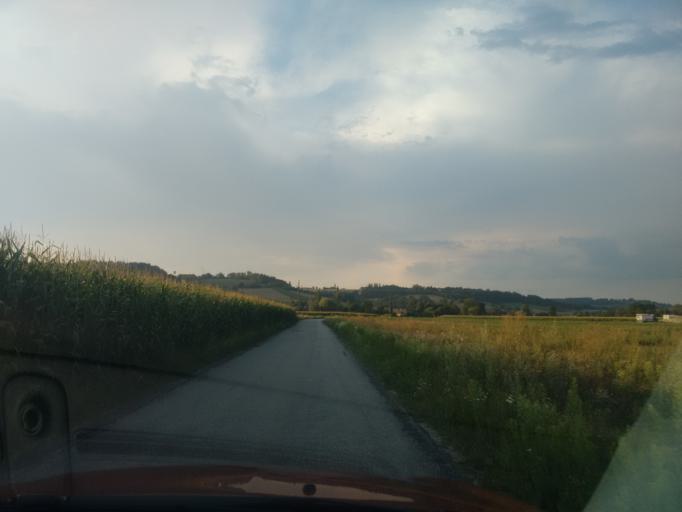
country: AT
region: Upper Austria
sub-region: Politischer Bezirk Grieskirchen
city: Bad Schallerbach
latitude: 48.2010
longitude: 13.9212
